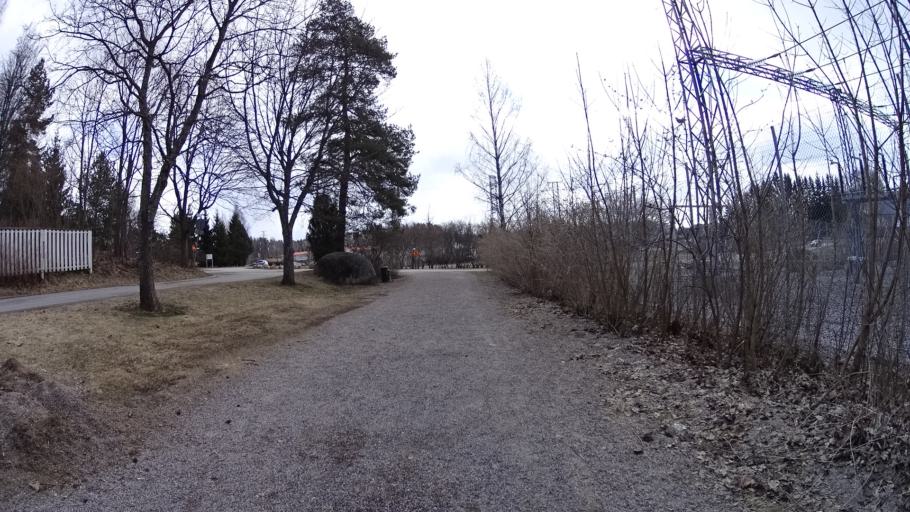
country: FI
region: Uusimaa
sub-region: Helsinki
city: Kilo
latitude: 60.2093
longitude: 24.7689
